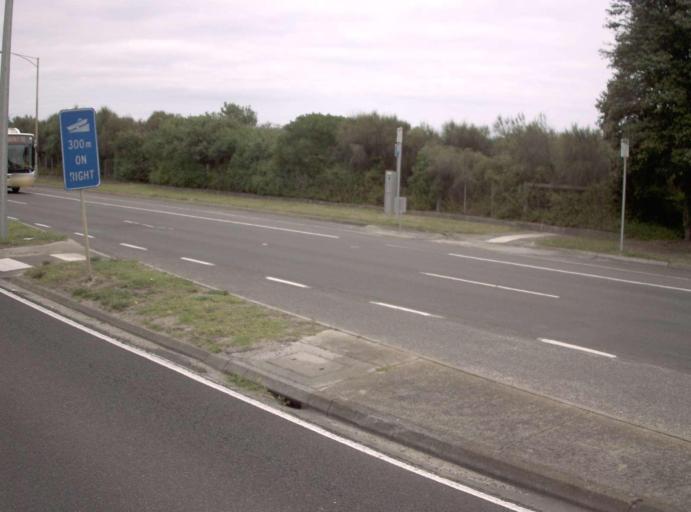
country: AU
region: Victoria
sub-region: Frankston
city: Frankston
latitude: -38.1506
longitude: 145.1144
